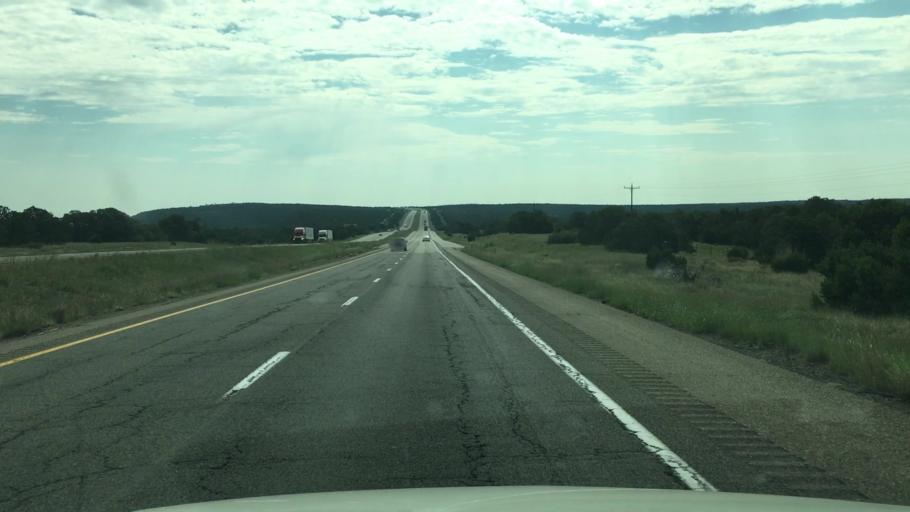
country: US
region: New Mexico
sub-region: Torrance County
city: Moriarty
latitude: 35.0036
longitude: -105.5855
